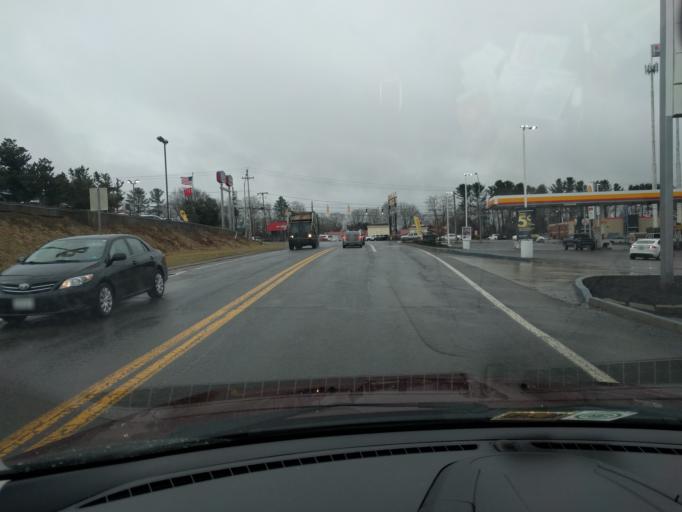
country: US
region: West Virginia
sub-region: Raleigh County
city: Mabscott
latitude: 37.7923
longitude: -81.2139
